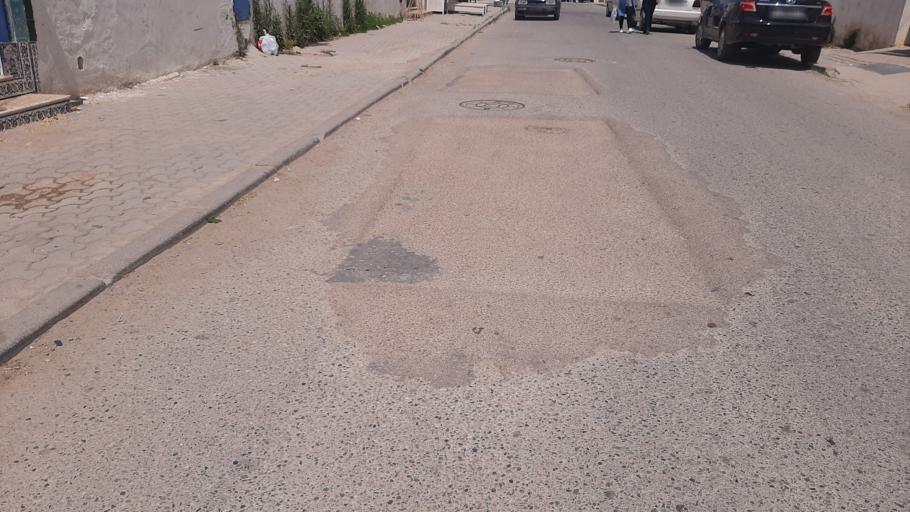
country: TN
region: Silyanah
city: Siliana
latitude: 36.0841
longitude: 9.3669
